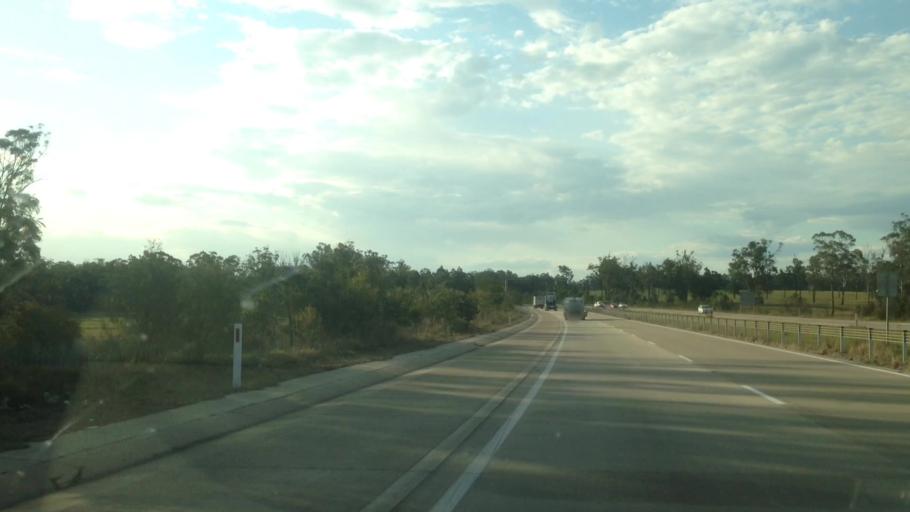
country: AU
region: New South Wales
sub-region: Cessnock
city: Heddon Greta
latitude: -32.8382
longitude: 151.5402
